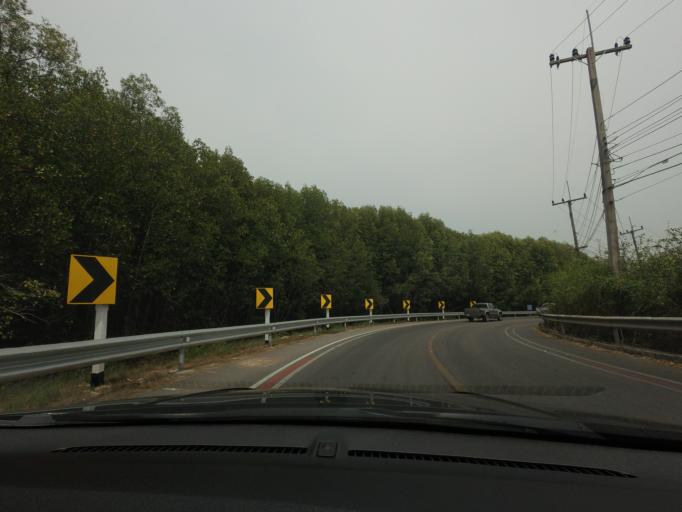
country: TH
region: Phetchaburi
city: Ban Laem
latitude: 13.2915
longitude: 99.9179
